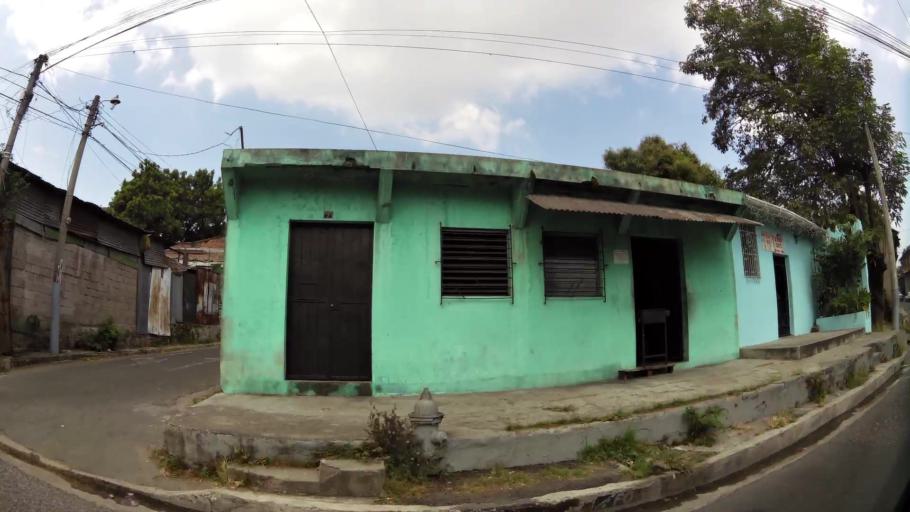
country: SV
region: San Salvador
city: Delgado
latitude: 13.7167
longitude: -89.1690
